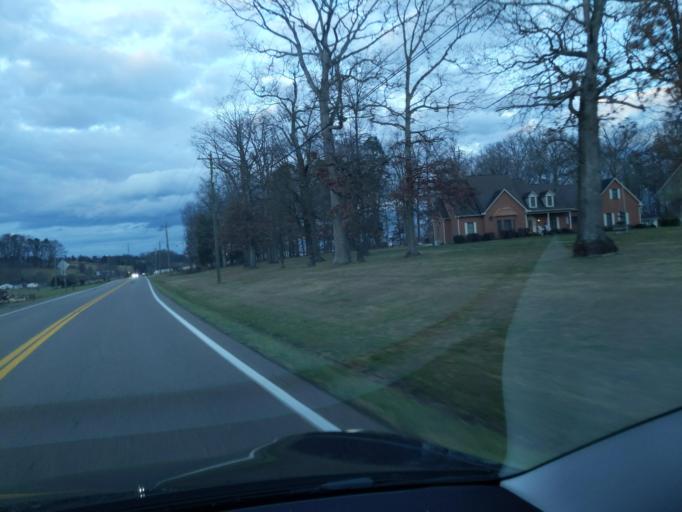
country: US
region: Tennessee
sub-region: Jefferson County
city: White Pine
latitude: 36.0973
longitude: -83.3563
